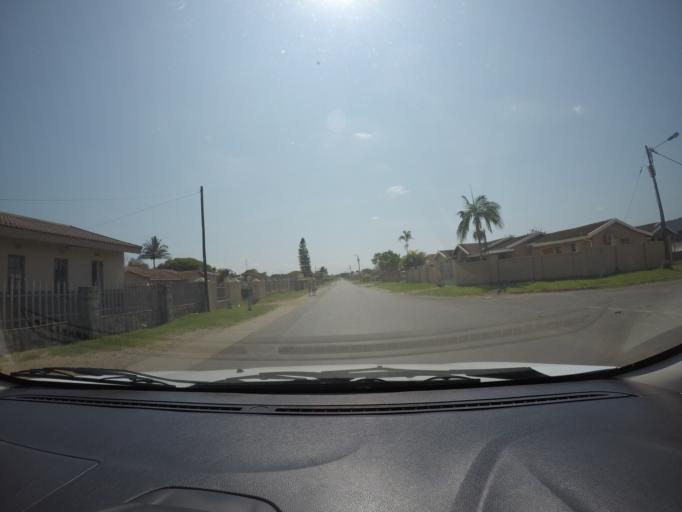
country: ZA
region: KwaZulu-Natal
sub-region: uThungulu District Municipality
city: eSikhawini
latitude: -28.8664
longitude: 31.9124
